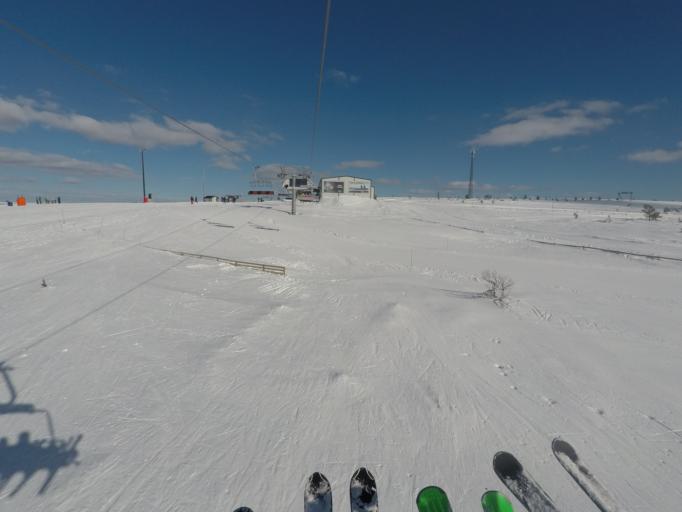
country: NO
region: Hedmark
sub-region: Trysil
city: Innbygda
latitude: 61.1749
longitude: 13.0150
